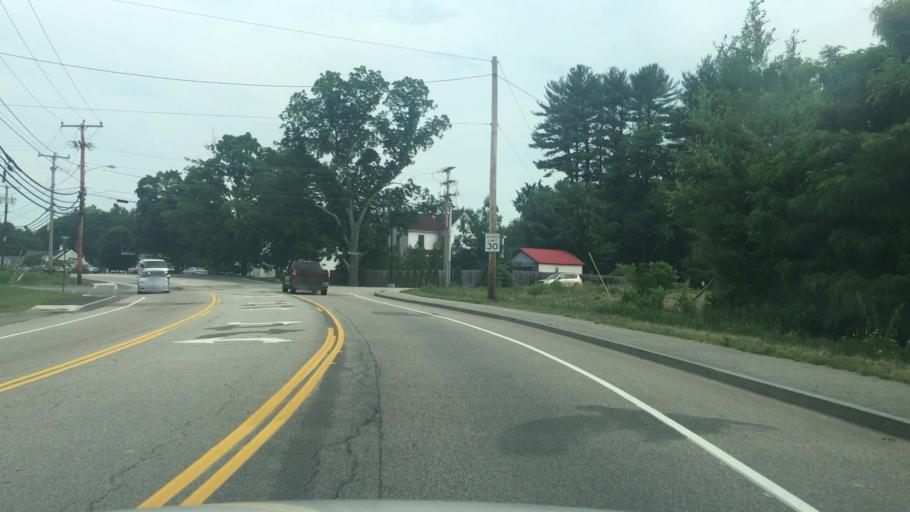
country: US
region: New Hampshire
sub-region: Rockingham County
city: Exeter
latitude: 42.9875
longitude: -70.9651
